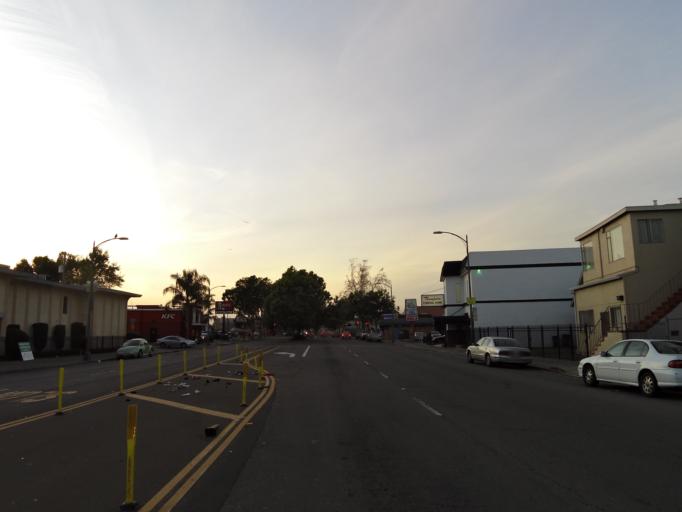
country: US
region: California
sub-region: Alameda County
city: San Leandro
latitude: 37.7432
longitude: -122.1696
